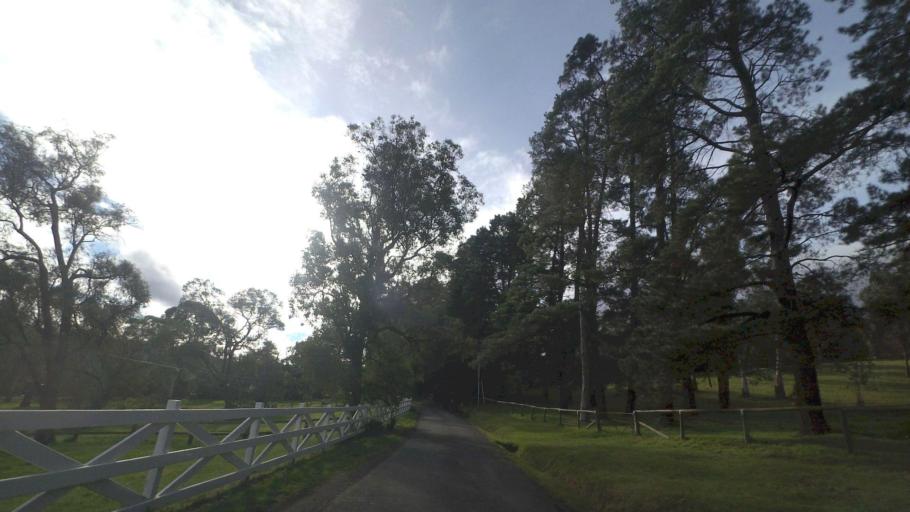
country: AU
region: Victoria
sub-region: Manningham
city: Warrandyte
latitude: -37.7376
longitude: 145.2319
